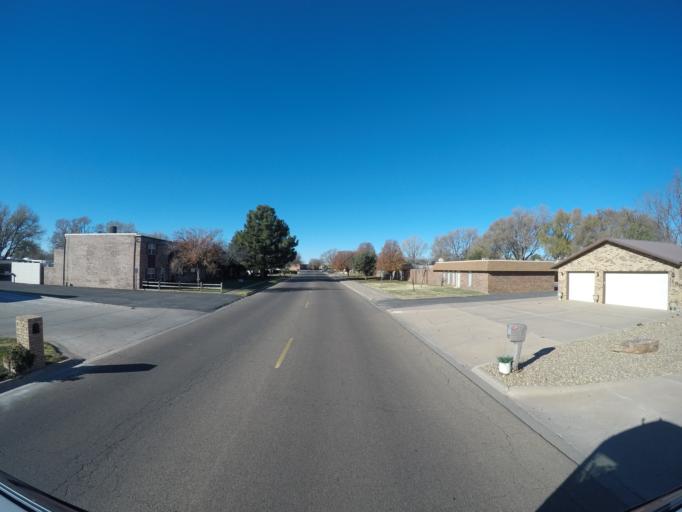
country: US
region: New Mexico
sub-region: Curry County
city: Clovis
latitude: 34.4414
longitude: -103.1864
